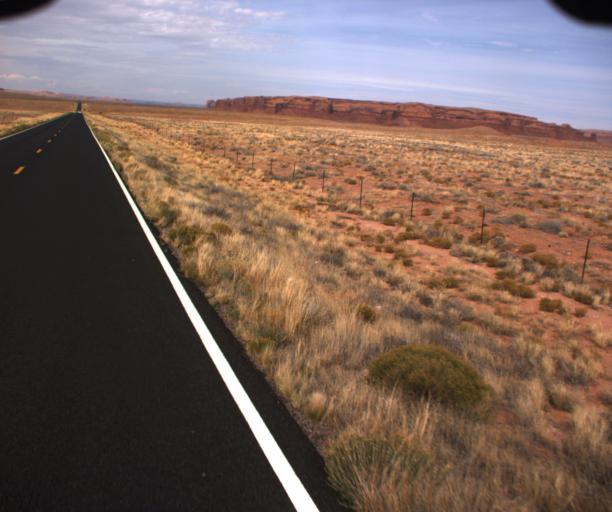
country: US
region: Arizona
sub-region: Apache County
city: Many Farms
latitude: 36.5716
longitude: -109.5482
